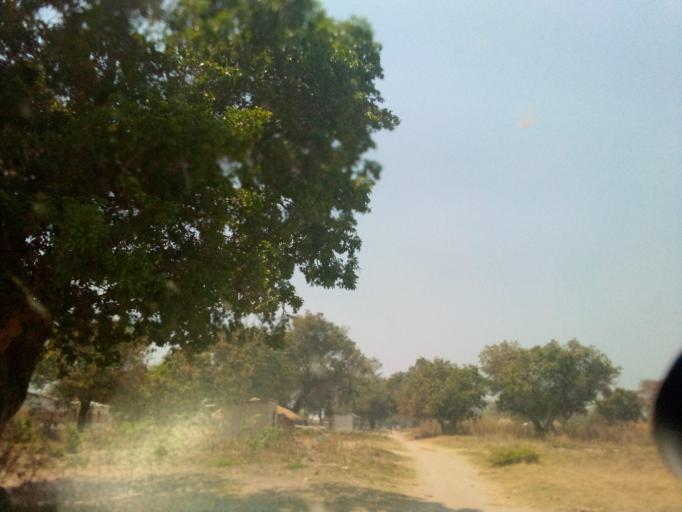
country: ZM
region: Copperbelt
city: Kataba
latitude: -12.2432
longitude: 30.3237
